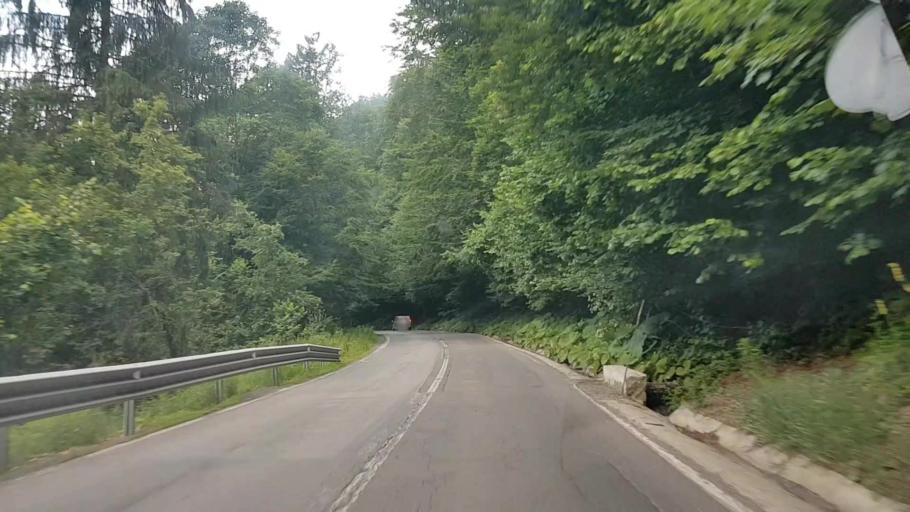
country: RO
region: Harghita
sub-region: Comuna Praid
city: Ocna de Sus
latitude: 46.6179
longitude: 25.2482
